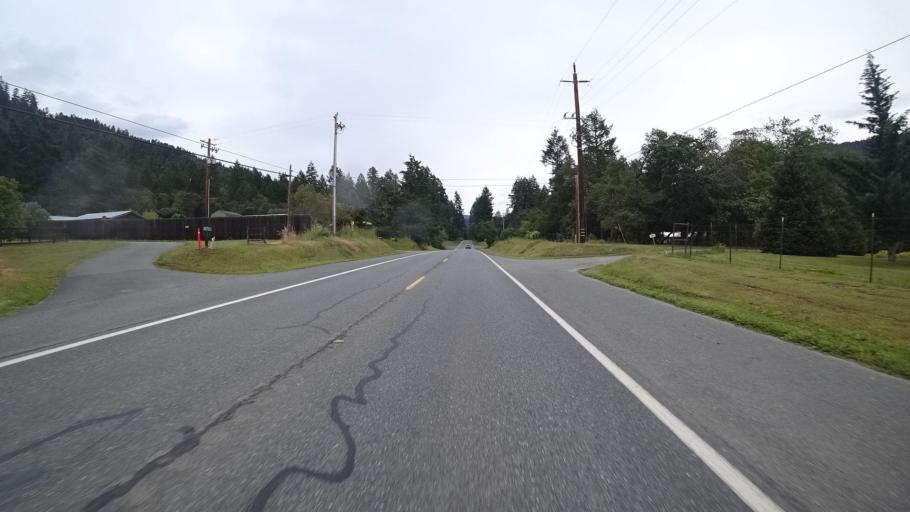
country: US
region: California
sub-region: Humboldt County
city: Willow Creek
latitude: 40.9612
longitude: -123.6425
